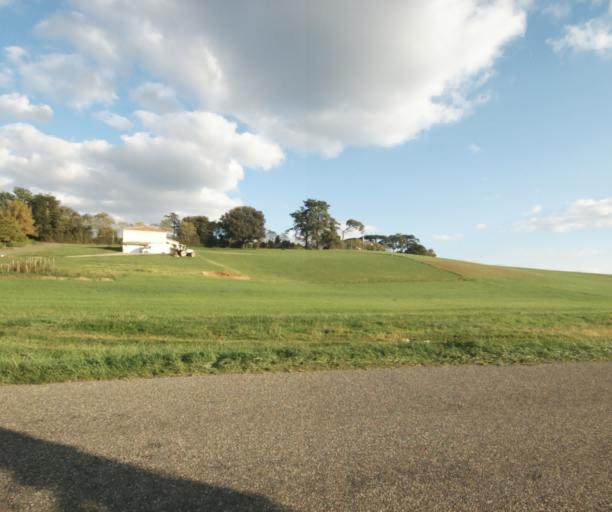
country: FR
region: Midi-Pyrenees
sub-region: Departement du Gers
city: Eauze
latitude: 43.7612
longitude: 0.1631
